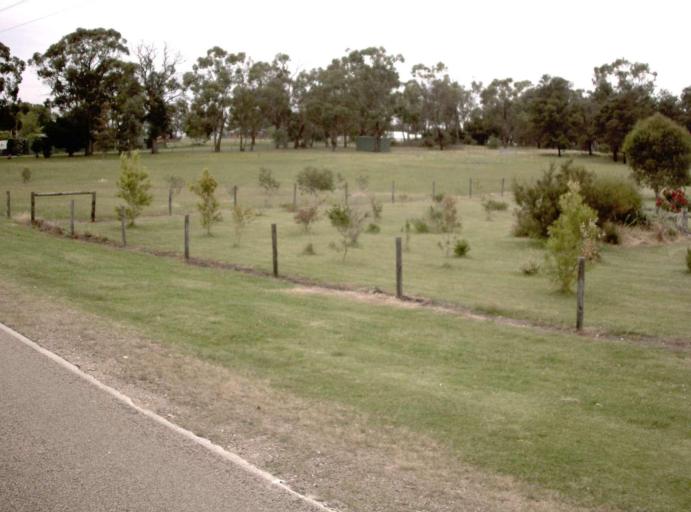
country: AU
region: Victoria
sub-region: East Gippsland
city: Bairnsdale
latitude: -37.8331
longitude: 147.4329
